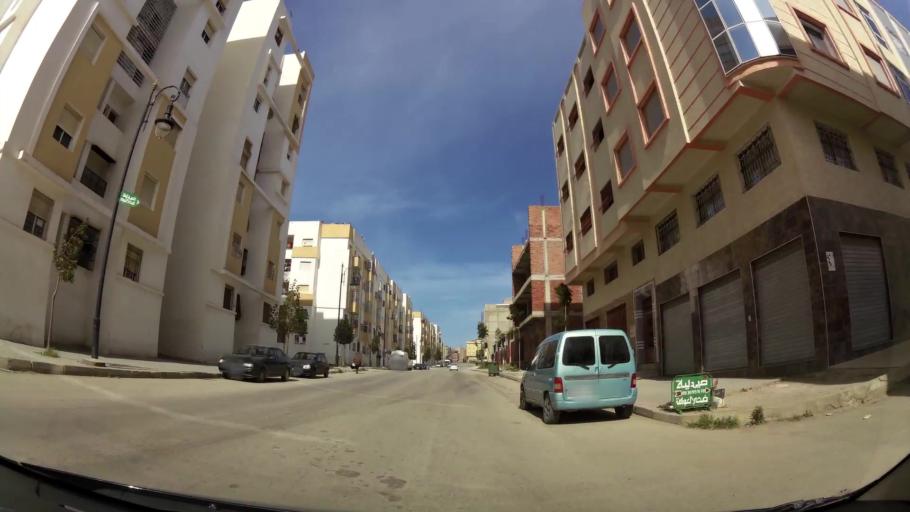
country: MA
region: Tanger-Tetouan
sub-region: Tanger-Assilah
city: Tangier
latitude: 35.7242
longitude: -5.8072
